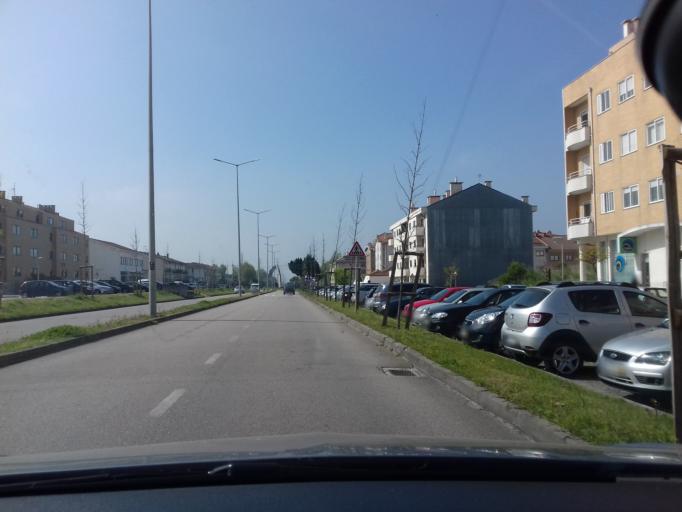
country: PT
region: Aveiro
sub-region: Espinho
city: Espinho
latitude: 41.0060
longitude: -8.6343
